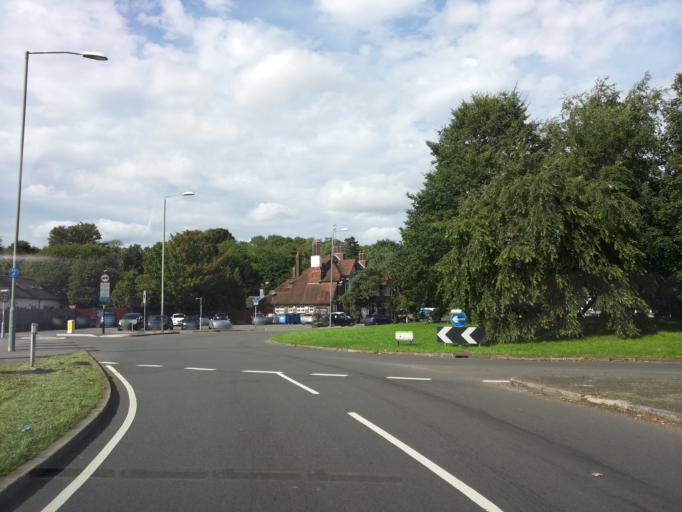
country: GB
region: England
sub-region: Greater London
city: Orpington
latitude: 51.3496
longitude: 0.0890
